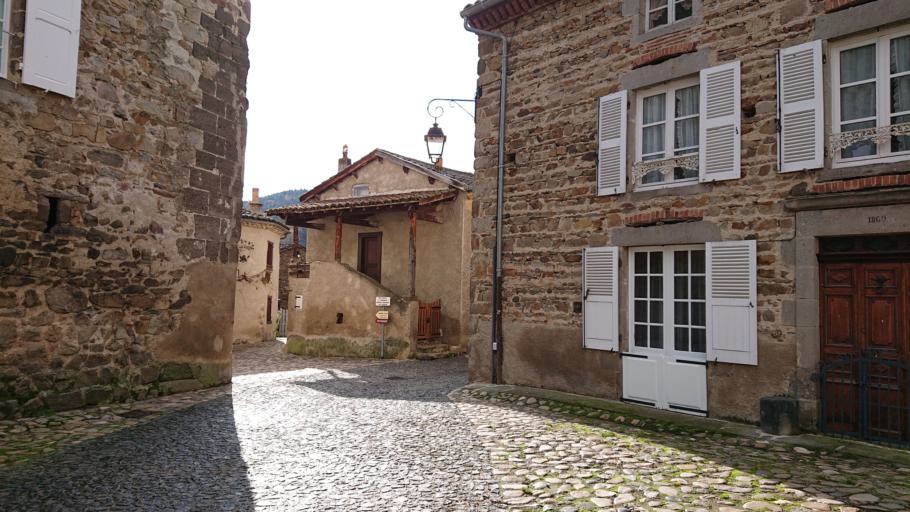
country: FR
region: Auvergne
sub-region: Departement de la Haute-Loire
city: Vieille-Brioude
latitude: 45.2623
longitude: 3.4540
